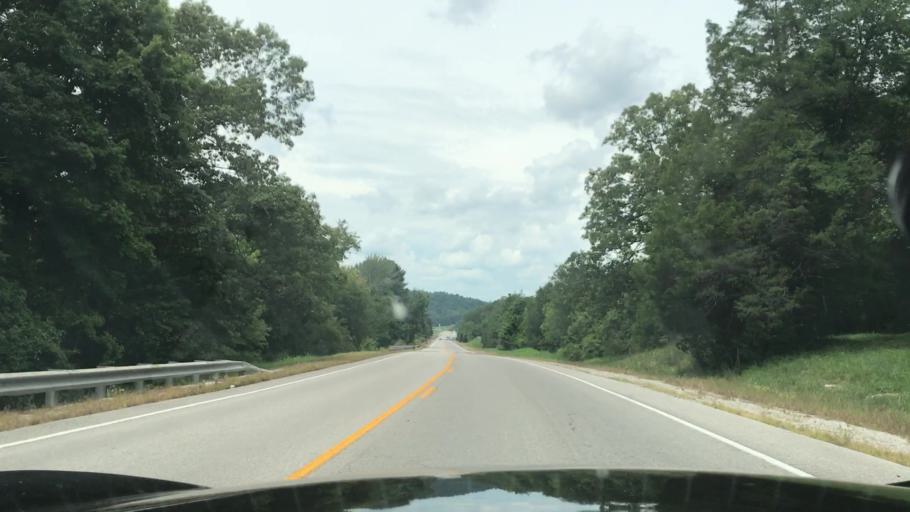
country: US
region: Kentucky
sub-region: Hart County
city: Horse Cave
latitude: 37.1944
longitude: -85.9257
